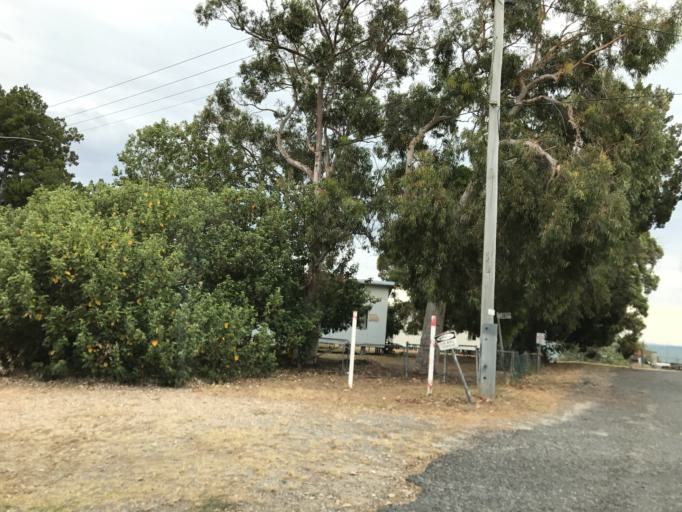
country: AU
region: Queensland
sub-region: Redland
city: Victoria Point
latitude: -27.5020
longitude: 153.4053
